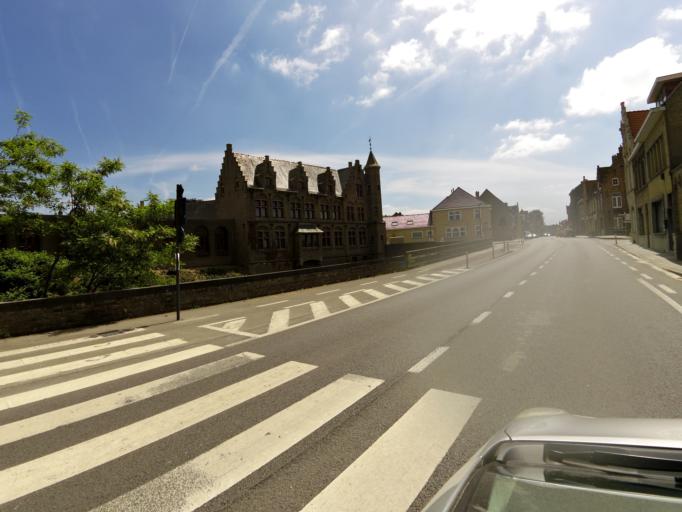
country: BE
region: Flanders
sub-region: Provincie West-Vlaanderen
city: Diksmuide
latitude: 51.0364
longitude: 2.8655
